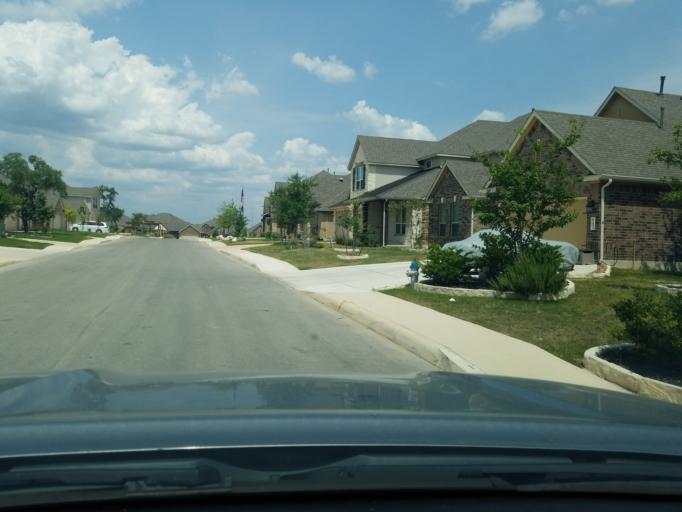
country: US
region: Texas
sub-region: Bexar County
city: Timberwood Park
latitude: 29.6821
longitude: -98.4801
